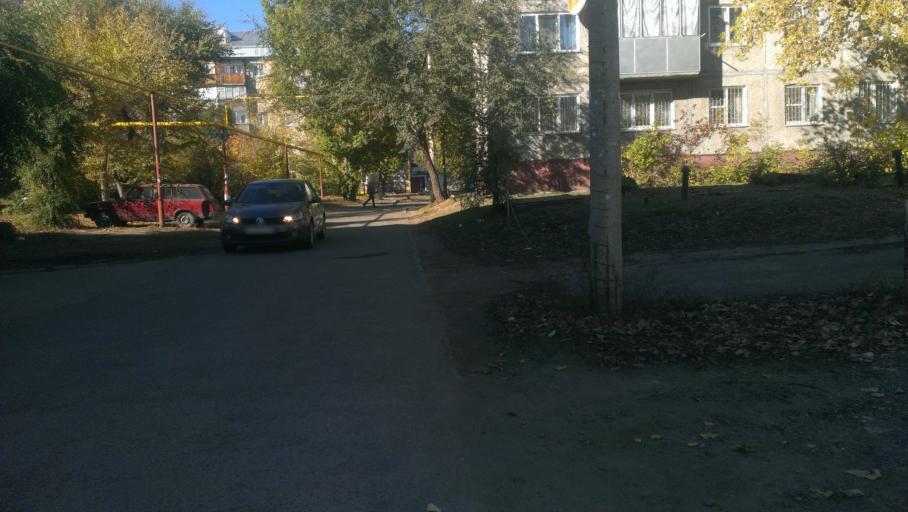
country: RU
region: Altai Krai
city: Novosilikatnyy
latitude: 53.3647
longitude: 83.6783
